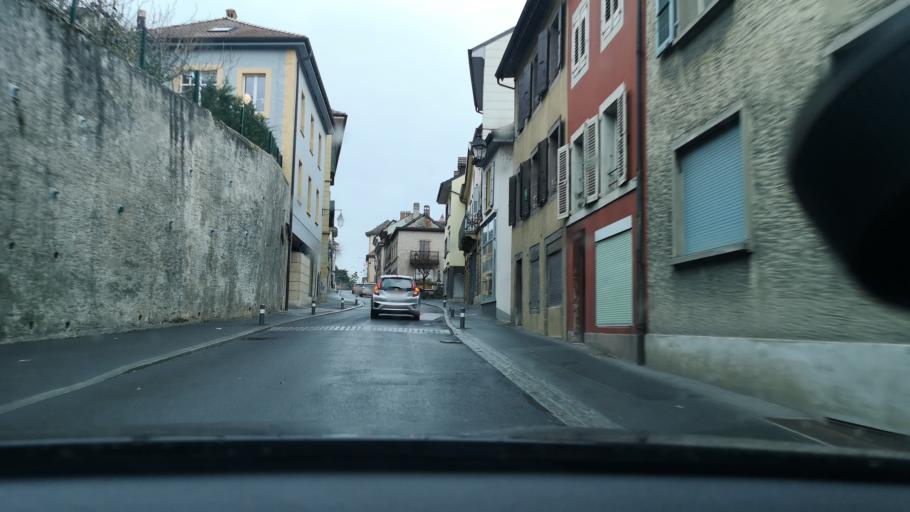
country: CH
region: Vaud
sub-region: Jura-Nord vaudois District
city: Grandson
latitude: 46.8079
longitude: 6.6442
